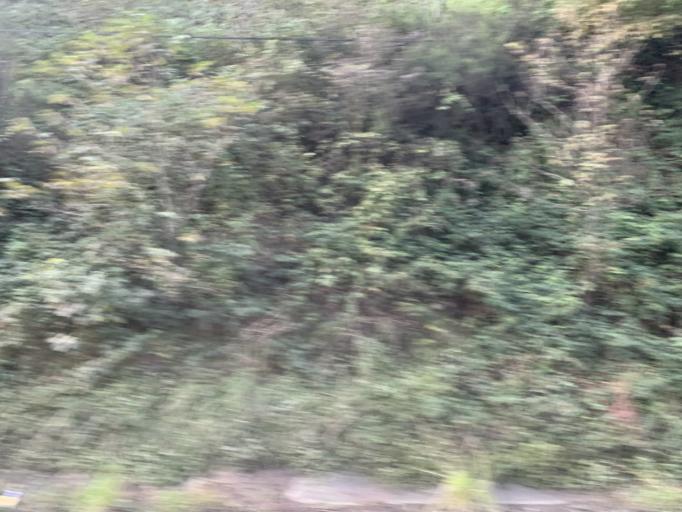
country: TR
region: Trabzon
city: Of
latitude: 40.8748
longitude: 40.2793
